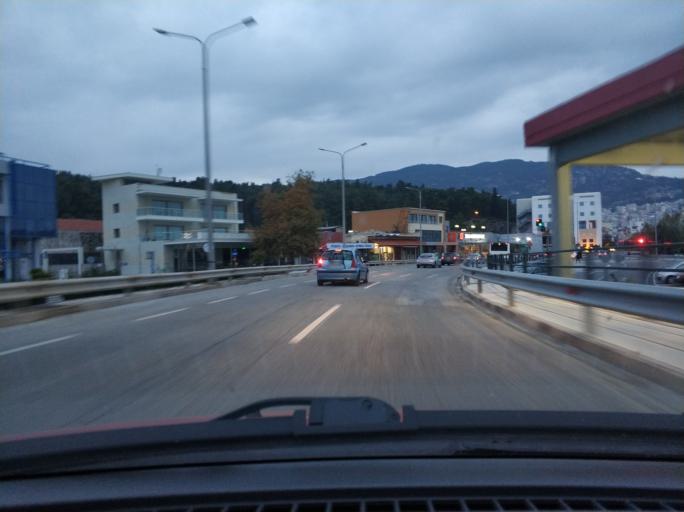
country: GR
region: East Macedonia and Thrace
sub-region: Nomos Kavalas
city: Kavala
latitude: 40.9278
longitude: 24.3908
